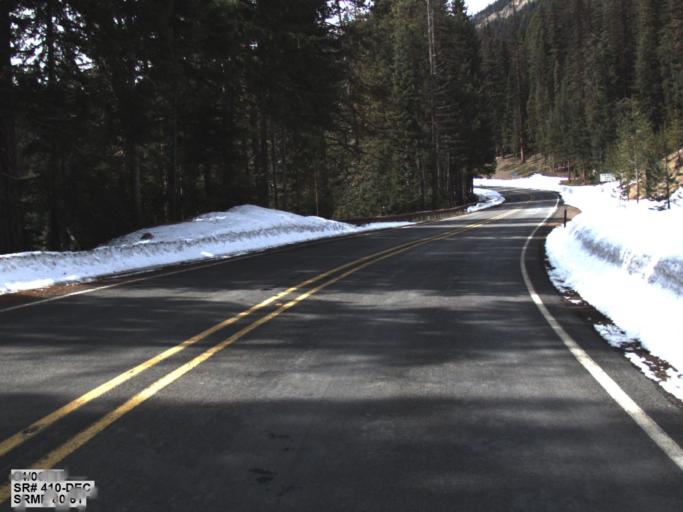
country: US
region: Washington
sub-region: Kittitas County
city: Cle Elum
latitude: 46.9465
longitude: -121.3209
